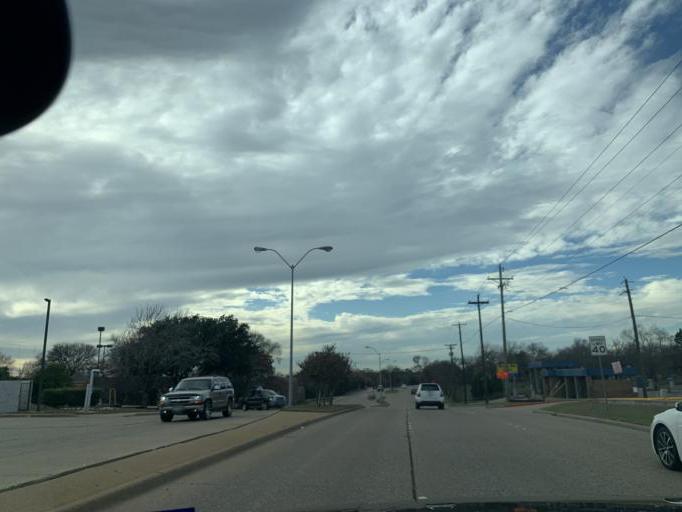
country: US
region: Texas
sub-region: Dallas County
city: Duncanville
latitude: 32.6330
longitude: -96.9016
